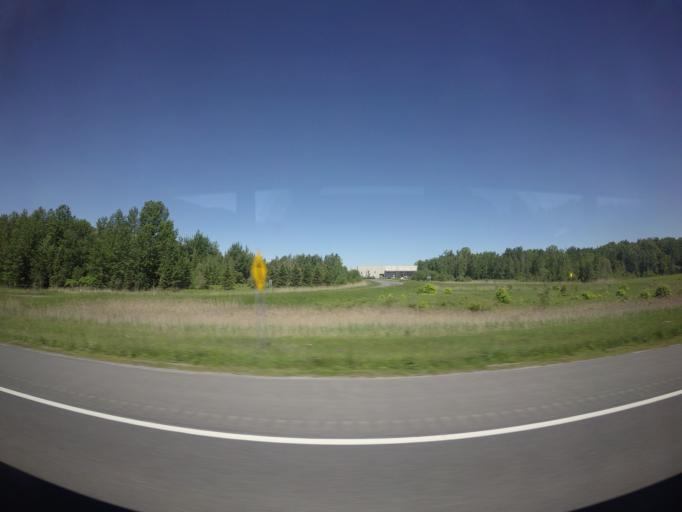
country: CA
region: Quebec
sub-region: Mauricie
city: Saint-Germain-de-Grantham
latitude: 45.7884
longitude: -72.6618
